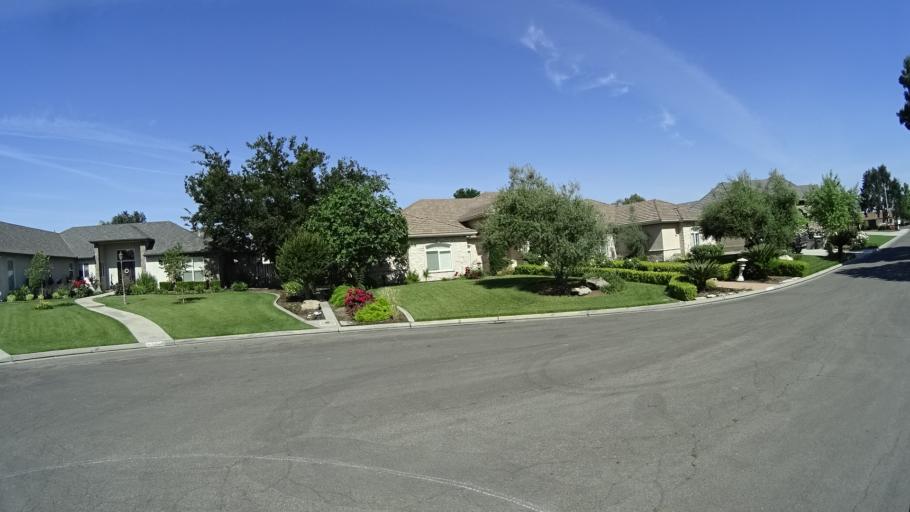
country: US
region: California
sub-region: Kings County
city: Lucerne
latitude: 36.3650
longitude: -119.6416
